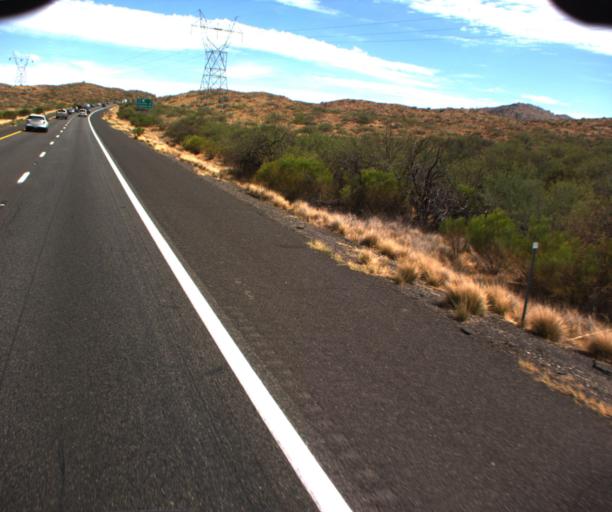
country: US
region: Arizona
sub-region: Yavapai County
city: Cordes Lakes
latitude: 34.2508
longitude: -112.1123
